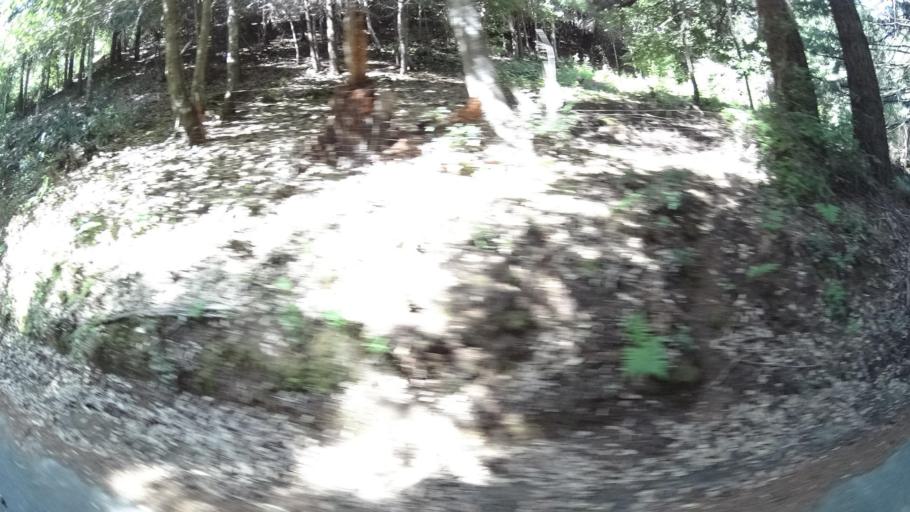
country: US
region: California
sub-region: Humboldt County
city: Redway
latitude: 40.1324
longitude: -123.9781
